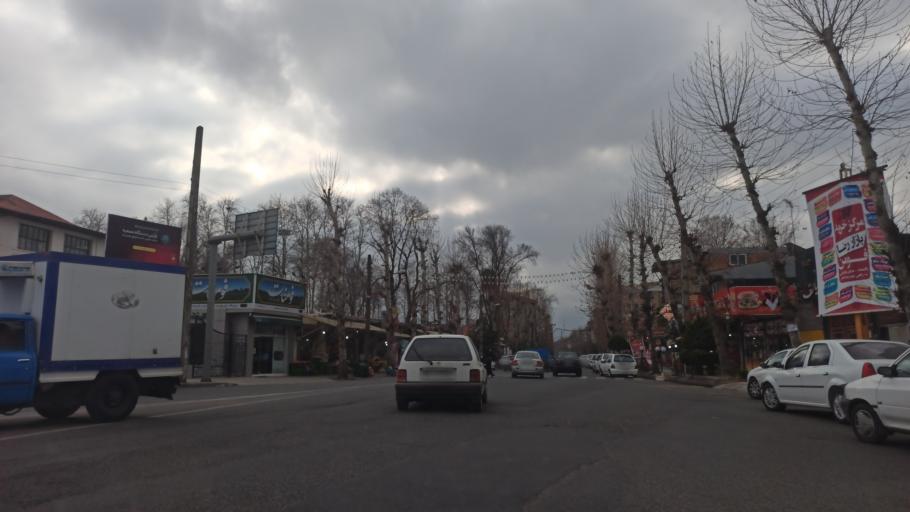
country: IR
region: Gilan
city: Fuman
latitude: 37.2325
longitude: 49.3187
